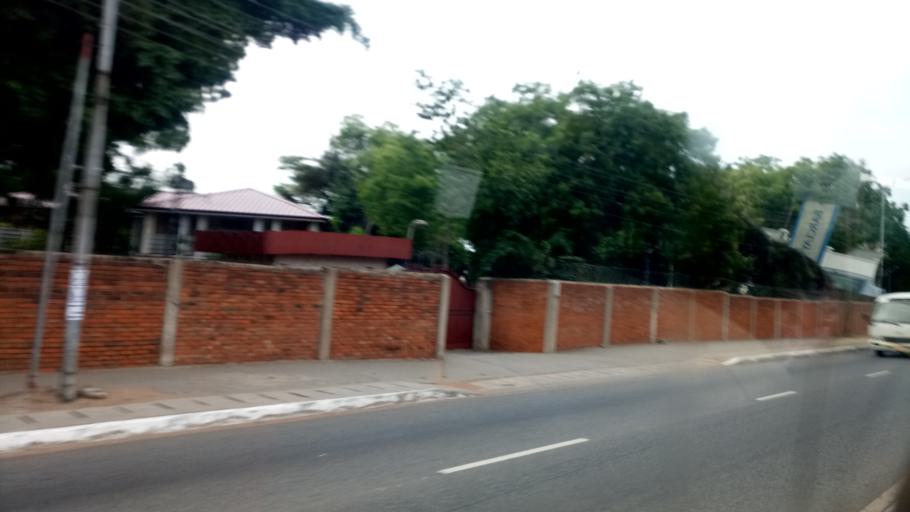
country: GH
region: Greater Accra
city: Accra
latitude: 5.5685
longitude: -0.1923
